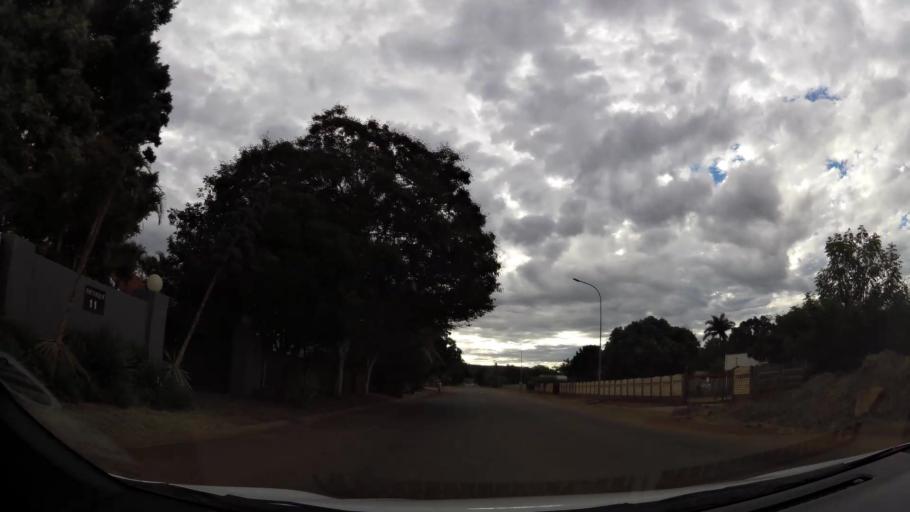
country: ZA
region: Limpopo
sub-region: Waterberg District Municipality
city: Modimolle
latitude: -24.5220
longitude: 28.7064
